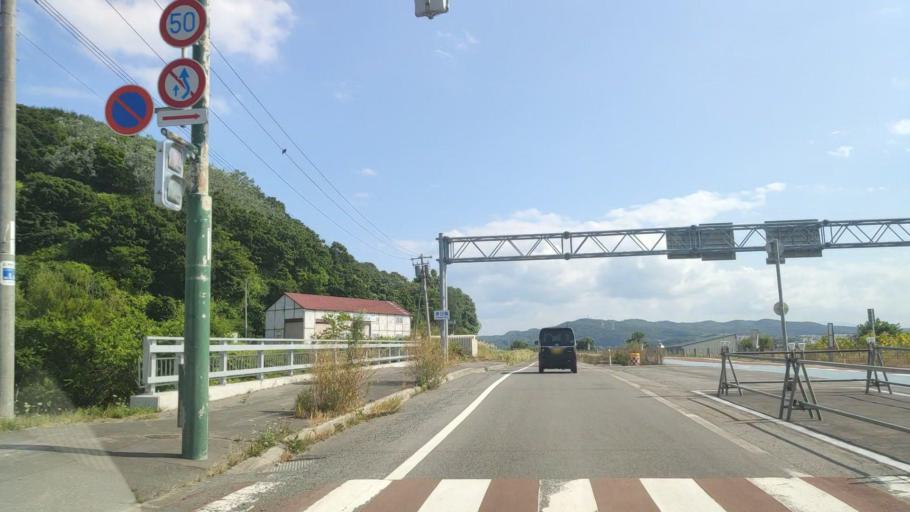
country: JP
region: Hokkaido
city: Rumoi
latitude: 43.9532
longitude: 141.6450
